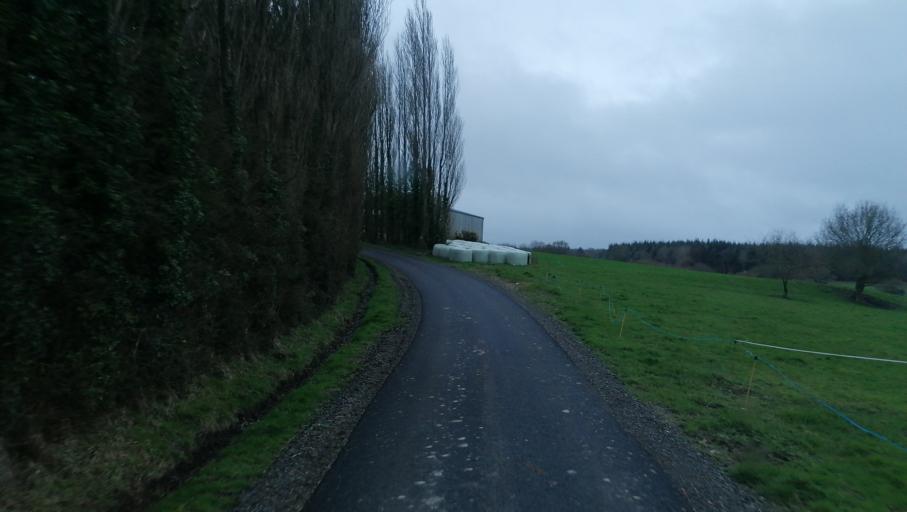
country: FR
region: Brittany
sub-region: Departement des Cotes-d'Armor
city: Saint-Agathon
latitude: 48.5657
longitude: -3.0621
